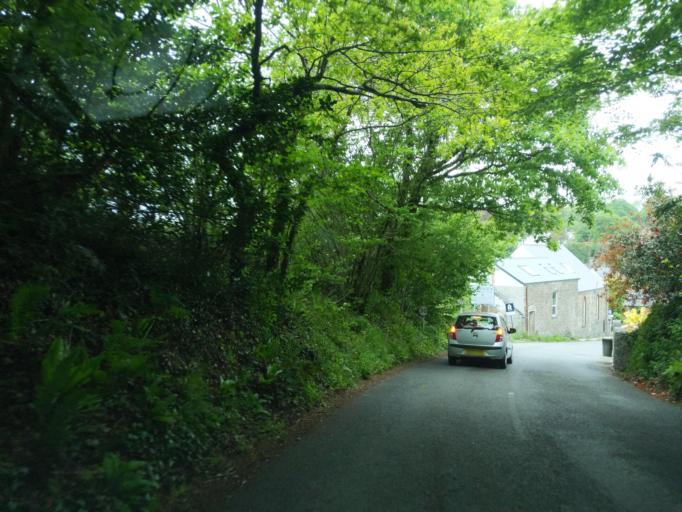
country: GB
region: England
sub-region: Devon
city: Tavistock
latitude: 50.5317
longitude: -4.1309
